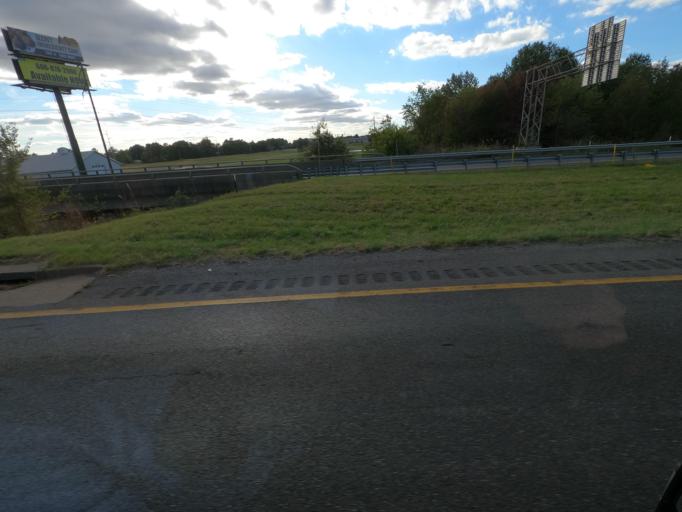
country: US
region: Illinois
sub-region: Massac County
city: Metropolis
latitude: 37.0909
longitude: -88.6856
